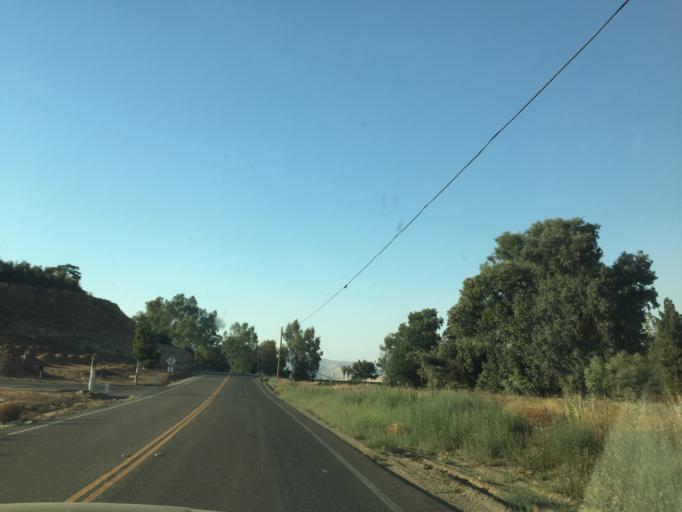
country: US
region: California
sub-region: Fresno County
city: Orange Cove
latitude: 36.5988
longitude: -119.2860
